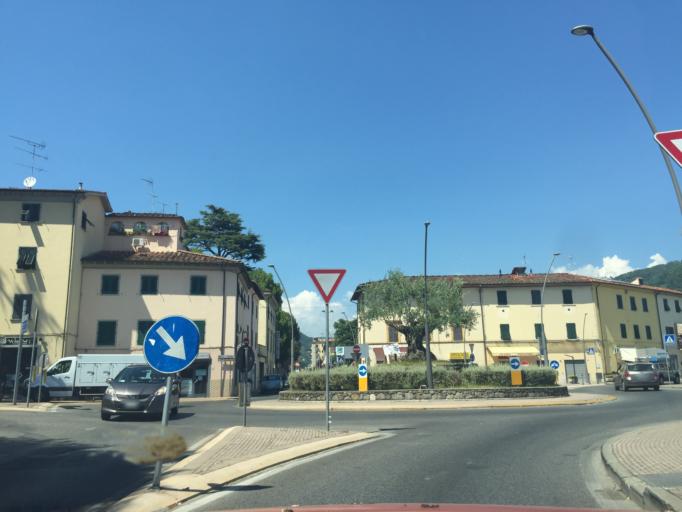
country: IT
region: Tuscany
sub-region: Provincia di Pistoia
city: Pescia
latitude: 43.8894
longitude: 10.6878
